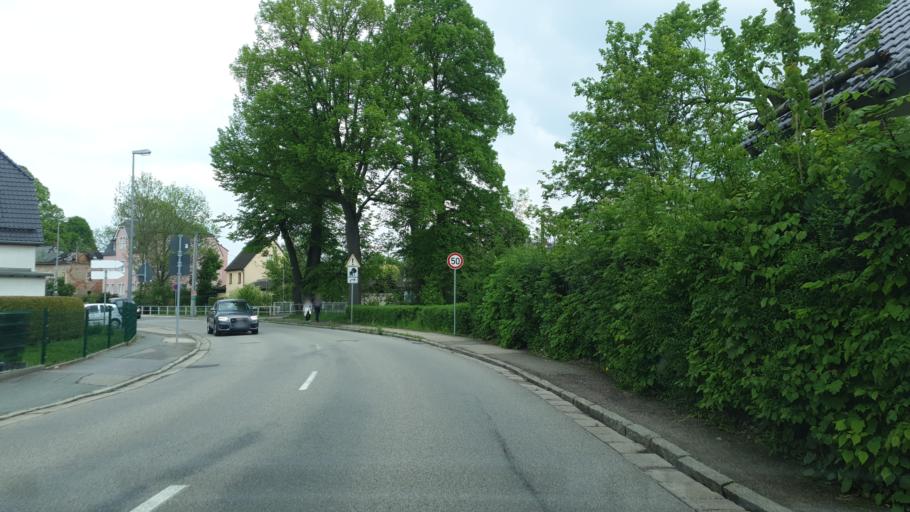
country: DE
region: Saxony
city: Wittgensdorf
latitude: 50.8611
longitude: 12.8354
